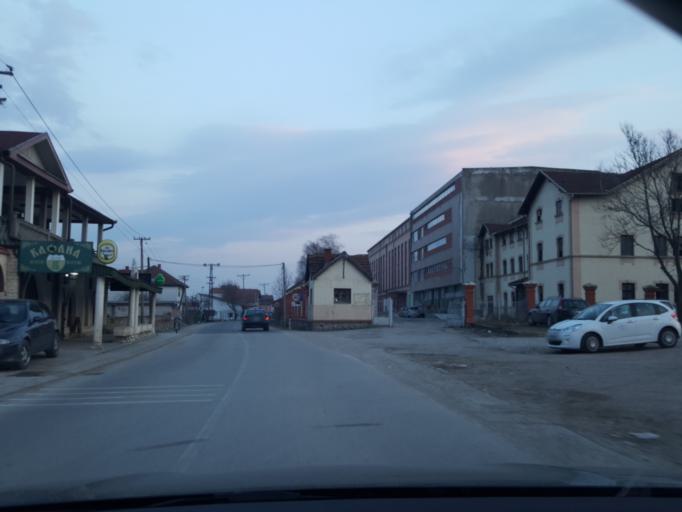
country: RS
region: Central Serbia
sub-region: Nisavski Okrug
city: Aleksinac
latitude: 43.5068
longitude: 21.6959
